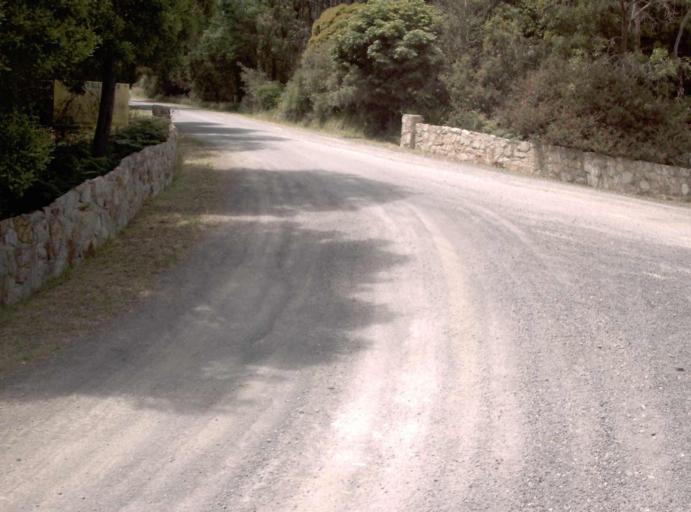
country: AU
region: Victoria
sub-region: Bass Coast
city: North Wonthaggi
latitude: -38.7263
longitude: 146.1214
